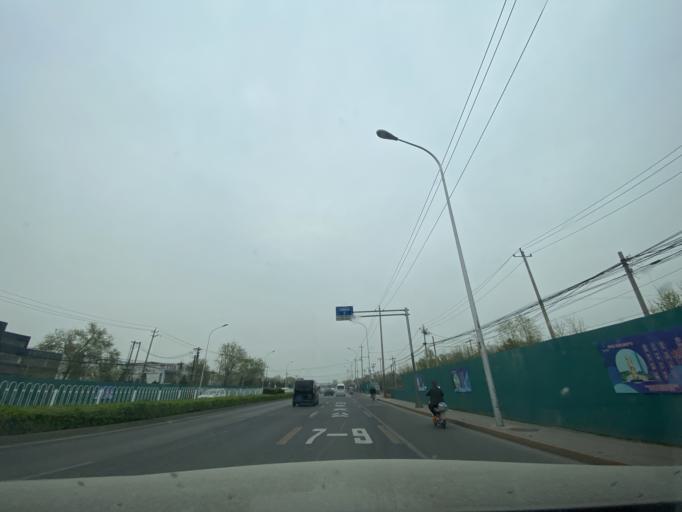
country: CN
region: Beijing
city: Sijiqing
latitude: 39.9456
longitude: 116.2512
